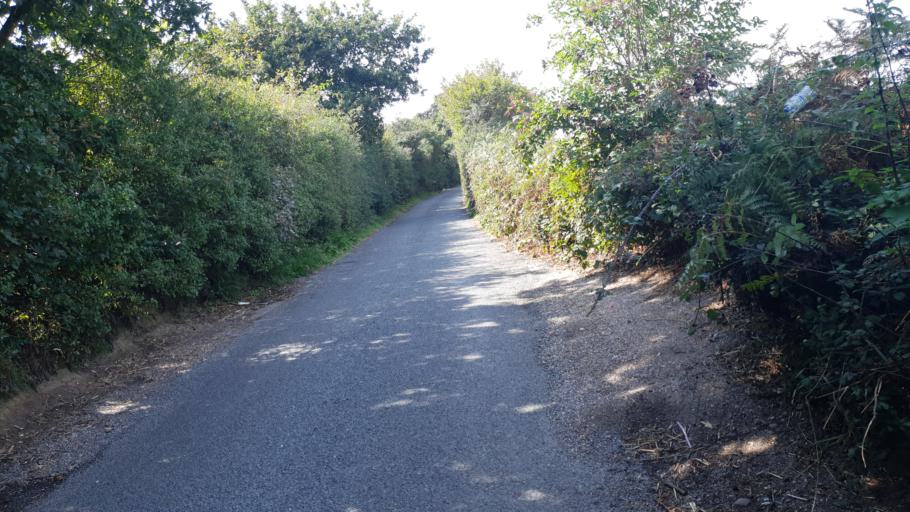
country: GB
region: England
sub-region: Essex
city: Colchester
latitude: 51.9276
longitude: 0.9613
